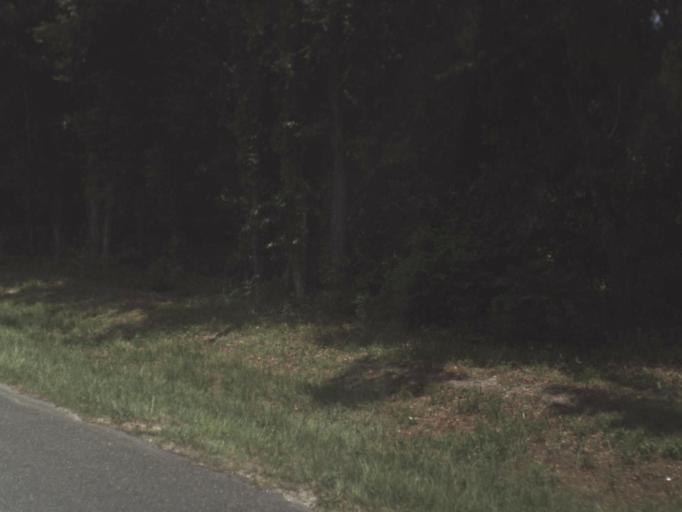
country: US
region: Florida
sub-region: Suwannee County
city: Wellborn
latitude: 30.0620
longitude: -82.7889
